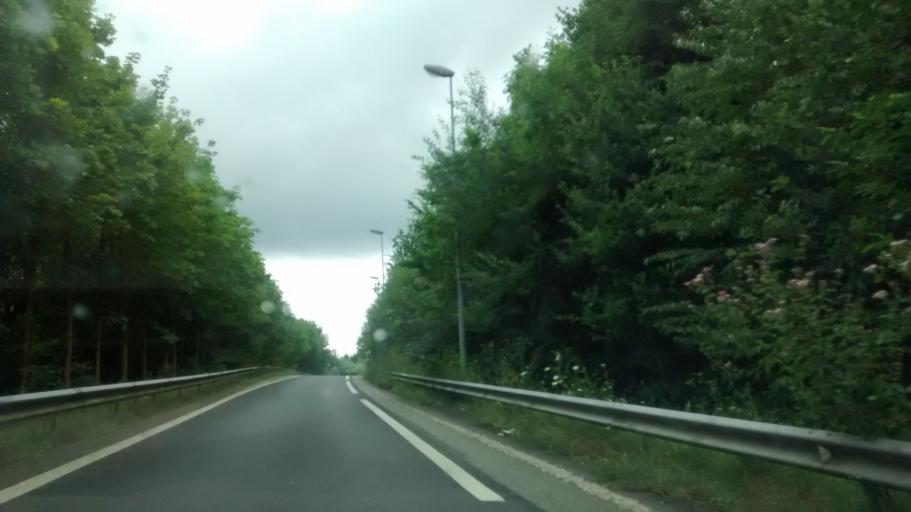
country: FR
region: Haute-Normandie
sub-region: Departement de la Seine-Maritime
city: Bois-Guillaume
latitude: 49.4654
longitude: 1.1358
